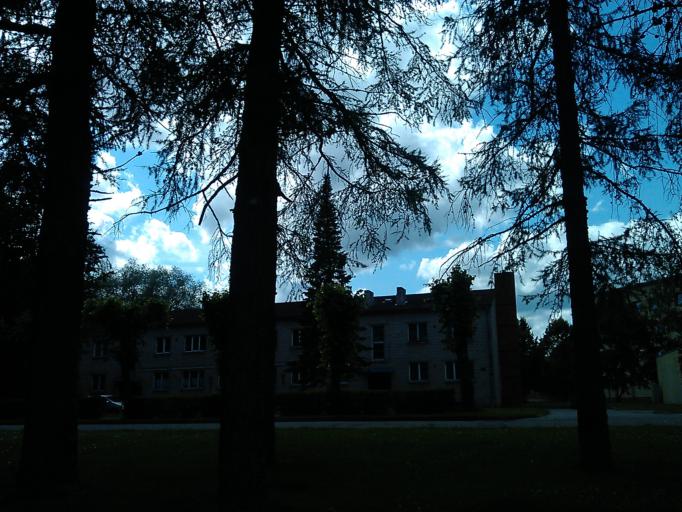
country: LV
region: Priekuli
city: Priekuli
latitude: 57.3120
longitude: 25.3608
